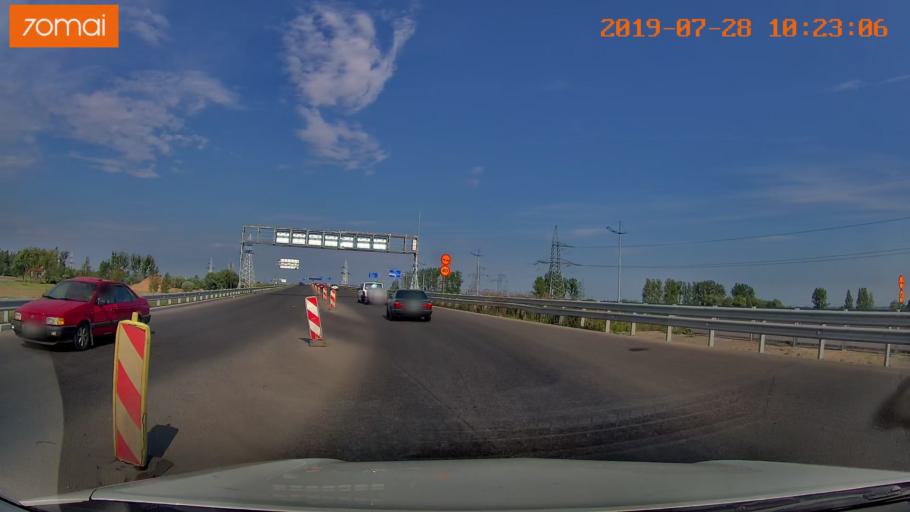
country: RU
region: Kaliningrad
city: Maloye Isakovo
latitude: 54.7652
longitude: 20.5636
